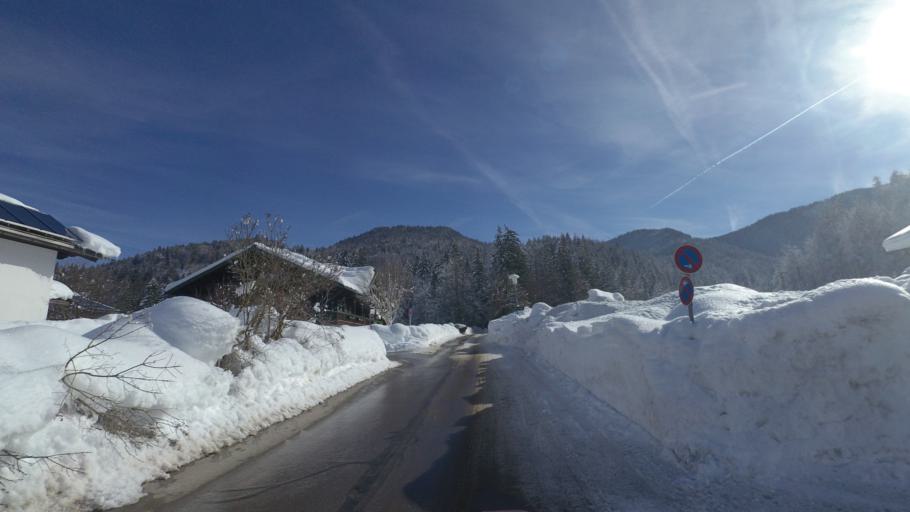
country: DE
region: Bavaria
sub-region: Upper Bavaria
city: Reit im Winkl
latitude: 47.6621
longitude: 12.4774
